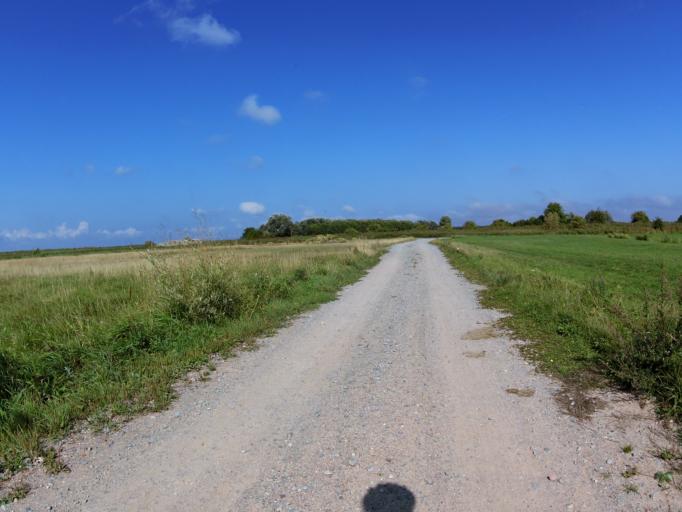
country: DE
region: Mecklenburg-Vorpommern
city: Loddin
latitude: 53.9789
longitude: 14.0517
